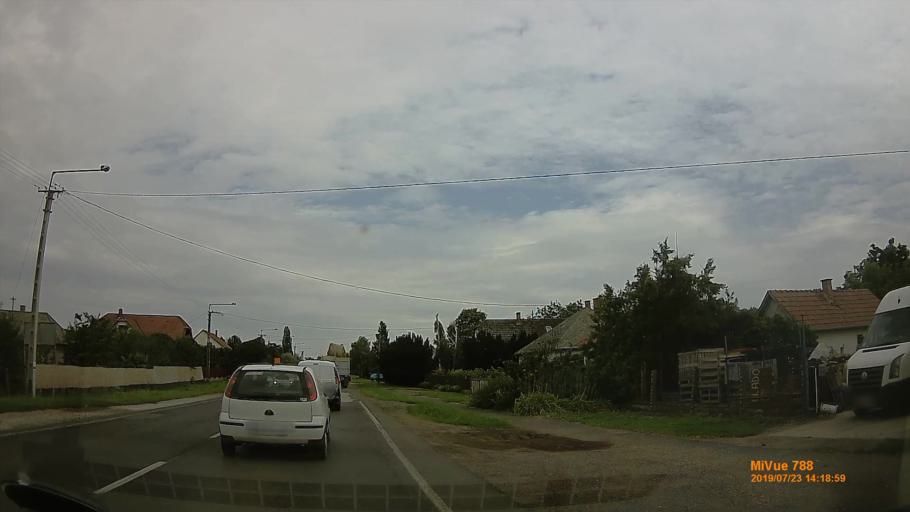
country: HU
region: Szabolcs-Szatmar-Bereg
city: Nagycserkesz
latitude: 47.9617
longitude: 21.5673
